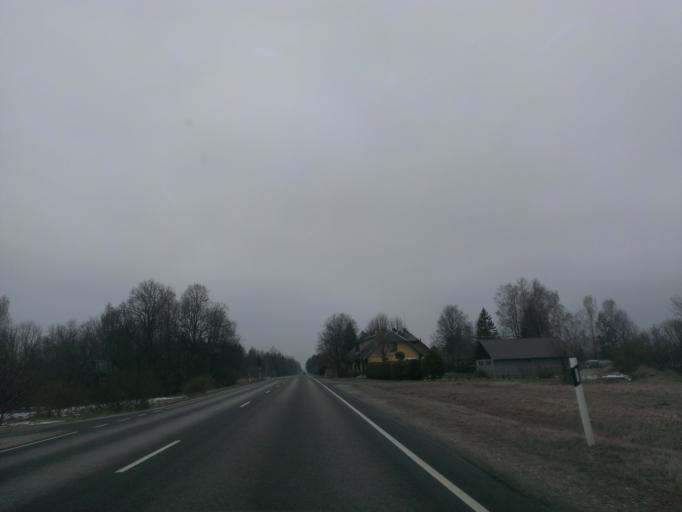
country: EE
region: Paernumaa
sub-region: Audru vald
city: Audru
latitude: 58.4298
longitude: 24.2821
